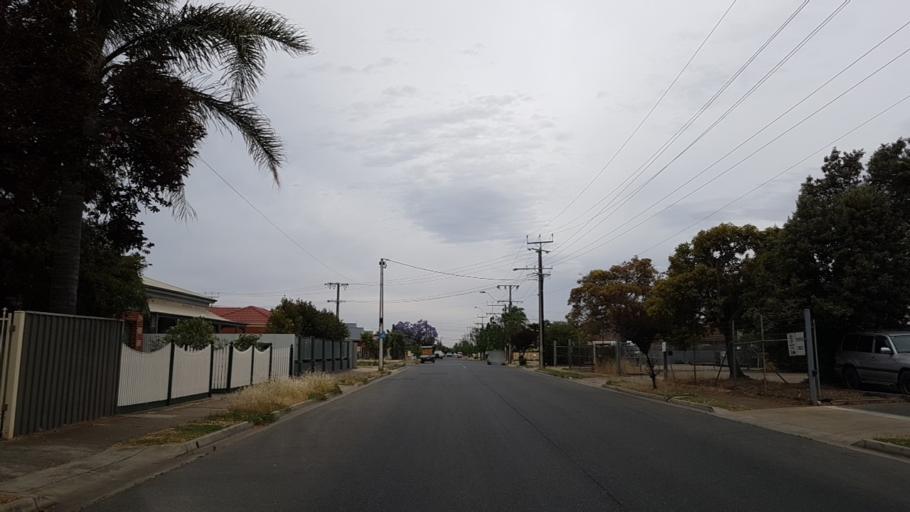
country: AU
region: South Australia
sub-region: Charles Sturt
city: Findon
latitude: -34.8952
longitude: 138.5413
